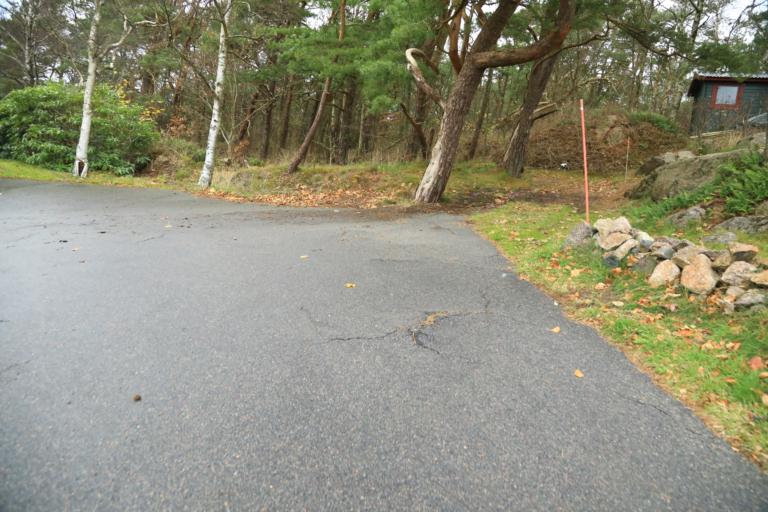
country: SE
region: Halland
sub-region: Varbergs Kommun
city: Varberg
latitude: 57.1711
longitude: 12.2082
